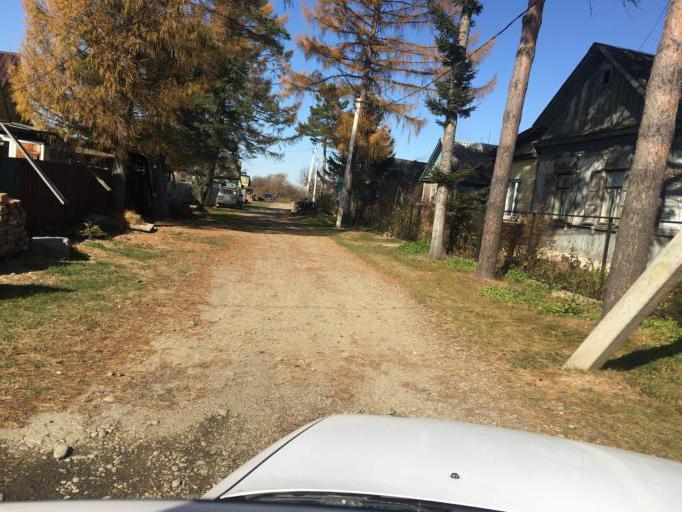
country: RU
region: Primorskiy
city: Dal'nerechensk
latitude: 45.9154
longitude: 133.7886
